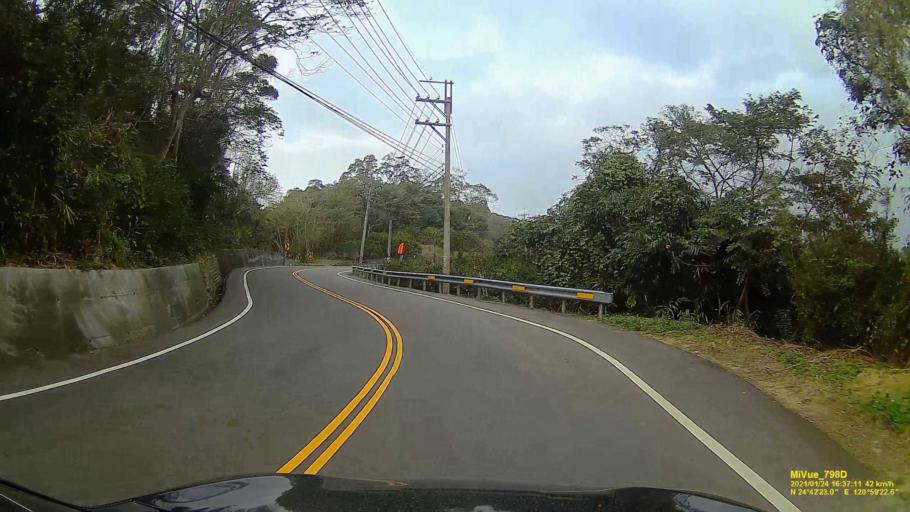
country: TW
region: Taiwan
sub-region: Hsinchu
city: Hsinchu
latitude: 24.7067
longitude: 120.9897
